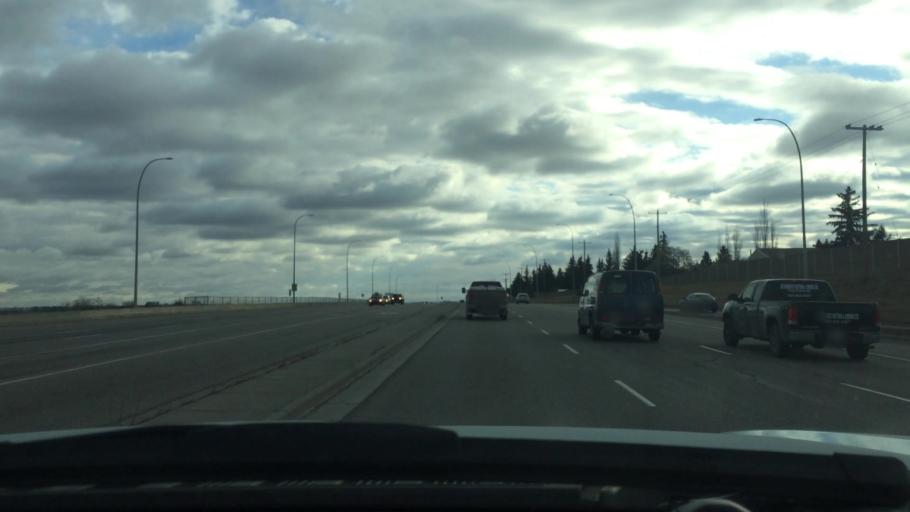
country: CA
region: Alberta
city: Calgary
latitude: 51.1381
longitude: -114.0814
